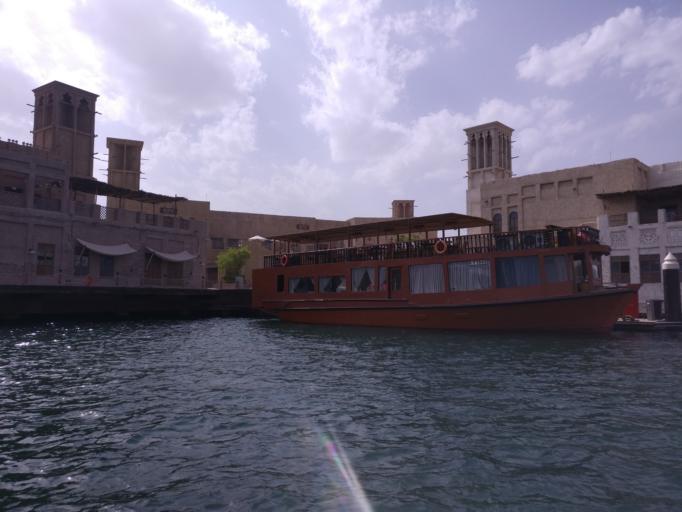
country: AE
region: Ash Shariqah
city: Sharjah
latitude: 25.2629
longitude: 55.3084
